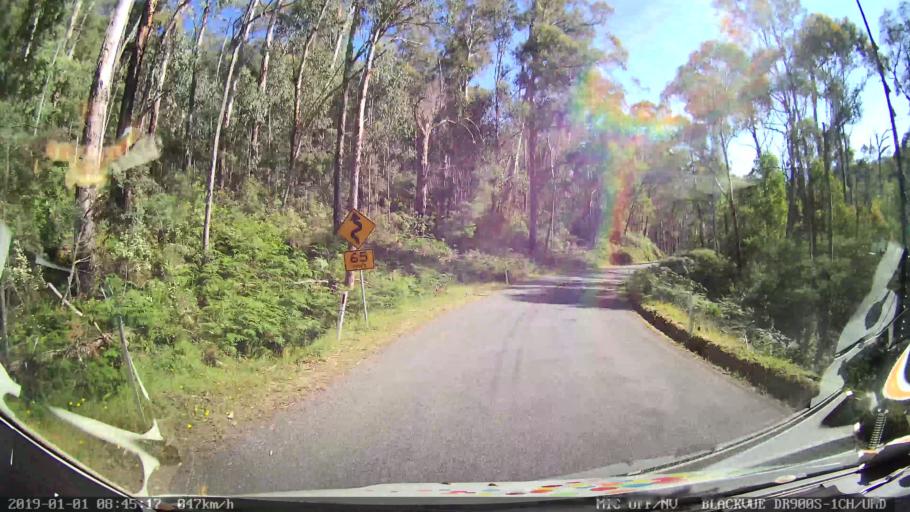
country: AU
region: New South Wales
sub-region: Snowy River
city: Jindabyne
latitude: -36.3064
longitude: 148.1877
